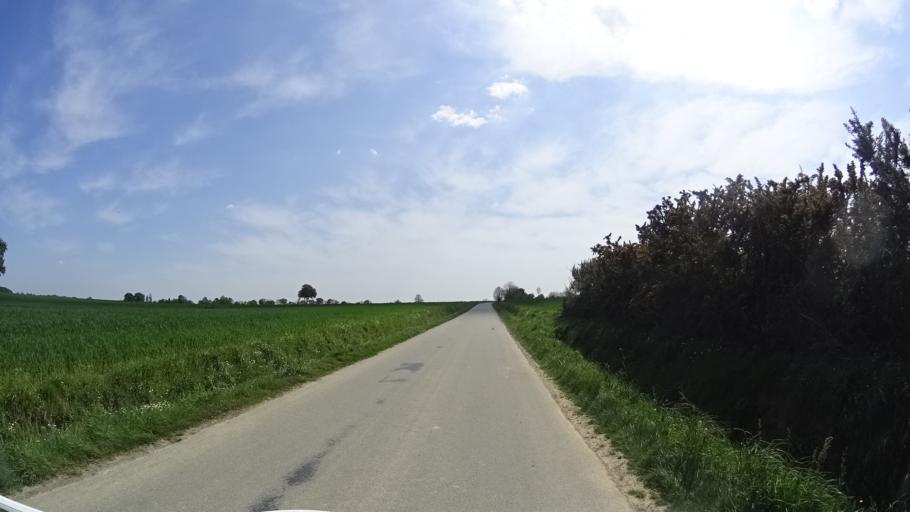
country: FR
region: Brittany
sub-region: Departement d'Ille-et-Vilaine
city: Torce
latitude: 48.0409
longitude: -1.2858
